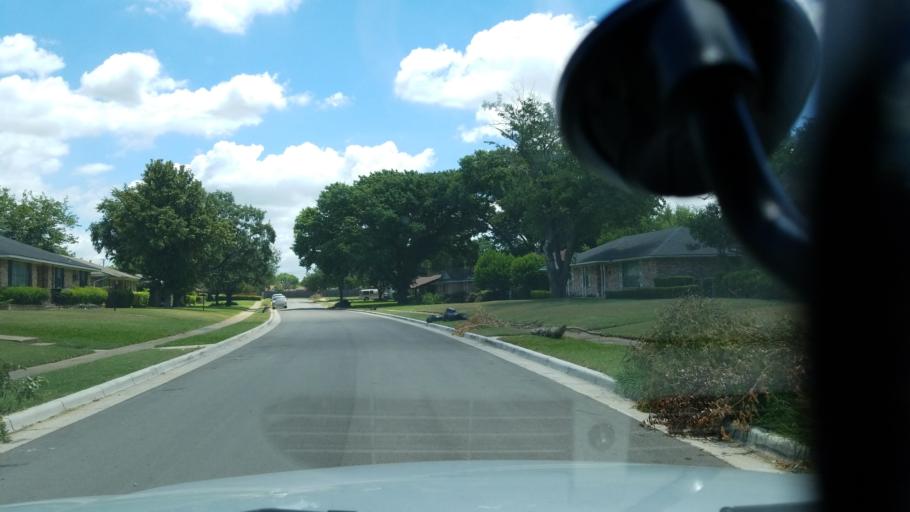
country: US
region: Texas
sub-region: Dallas County
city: Duncanville
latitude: 32.6682
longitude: -96.8591
